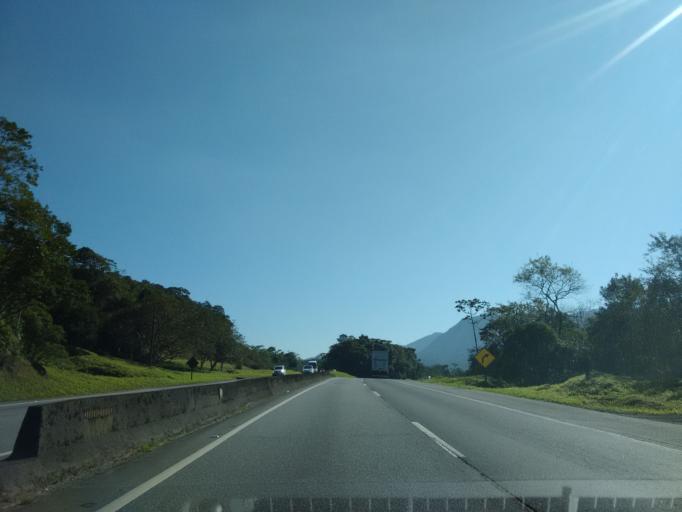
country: BR
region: Parana
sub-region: Guaratuba
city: Guaratuba
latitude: -25.9473
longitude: -48.9071
